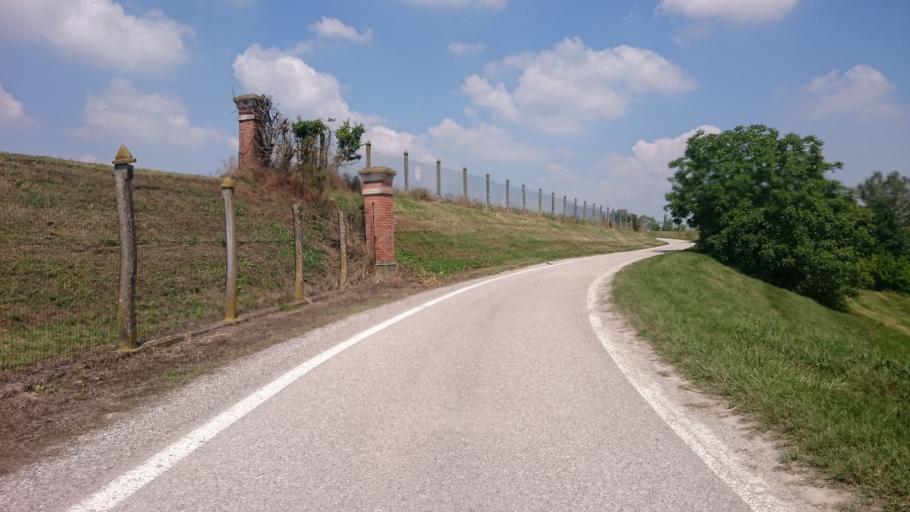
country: IT
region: Lombardy
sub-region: Provincia di Mantova
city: Bagnolo San Vito
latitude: 45.1005
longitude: 10.8896
